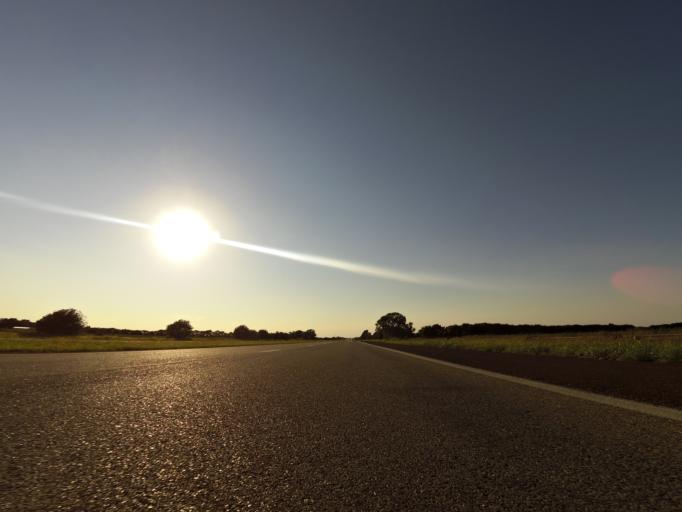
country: US
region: Kansas
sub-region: Reno County
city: Haven
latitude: 37.9171
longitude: -97.8232
